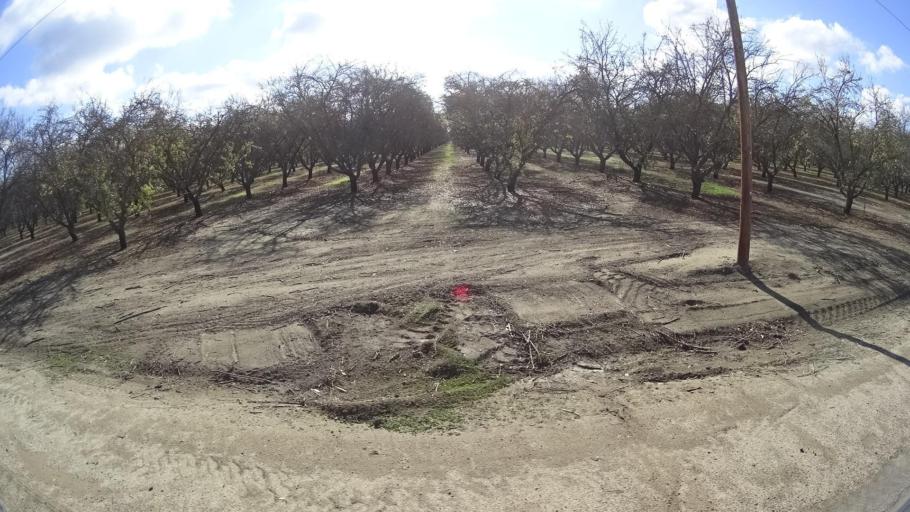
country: US
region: California
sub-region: Kern County
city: McFarland
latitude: 35.6887
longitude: -119.2931
